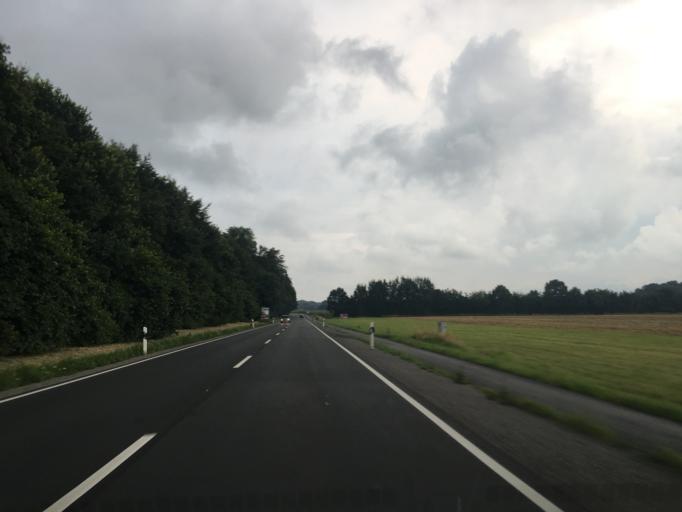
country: DE
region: North Rhine-Westphalia
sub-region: Regierungsbezirk Munster
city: Muenster
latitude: 52.0173
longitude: 7.6161
